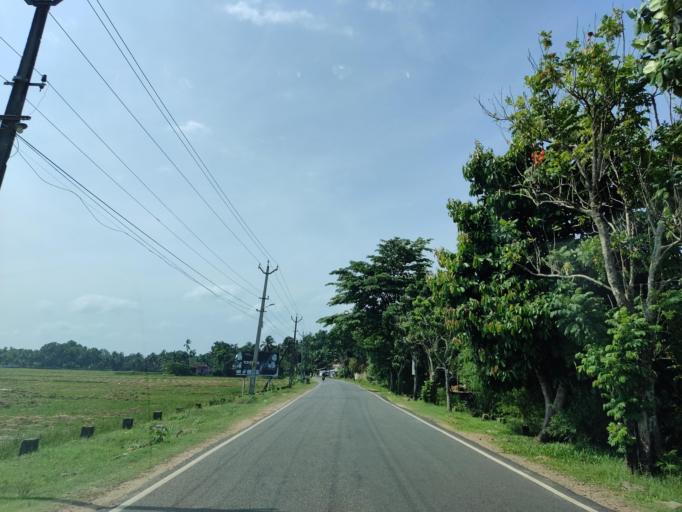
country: IN
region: Kerala
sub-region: Pattanamtitta
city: Tiruvalla
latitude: 9.3505
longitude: 76.4694
